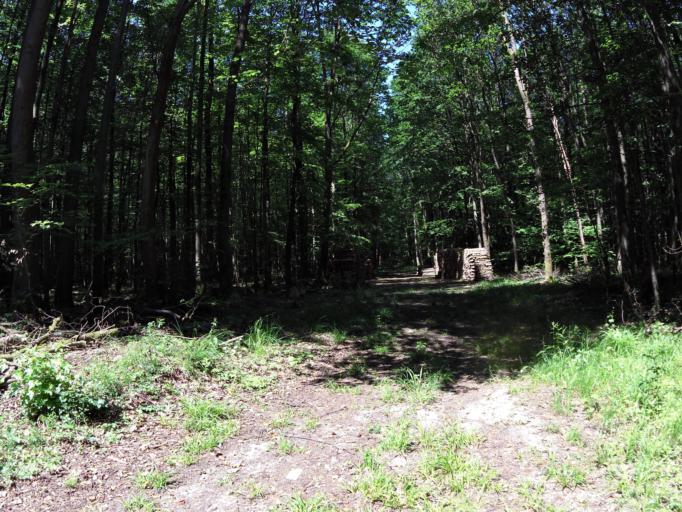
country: DE
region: Bavaria
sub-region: Regierungsbezirk Unterfranken
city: Kist
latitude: 49.7254
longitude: 9.8688
